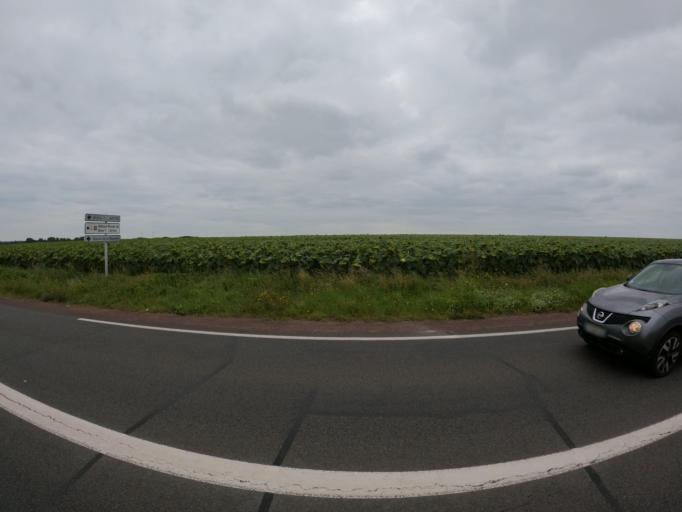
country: FR
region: Pays de la Loire
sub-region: Departement de la Vendee
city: Maillezais
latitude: 46.4170
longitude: -0.7007
